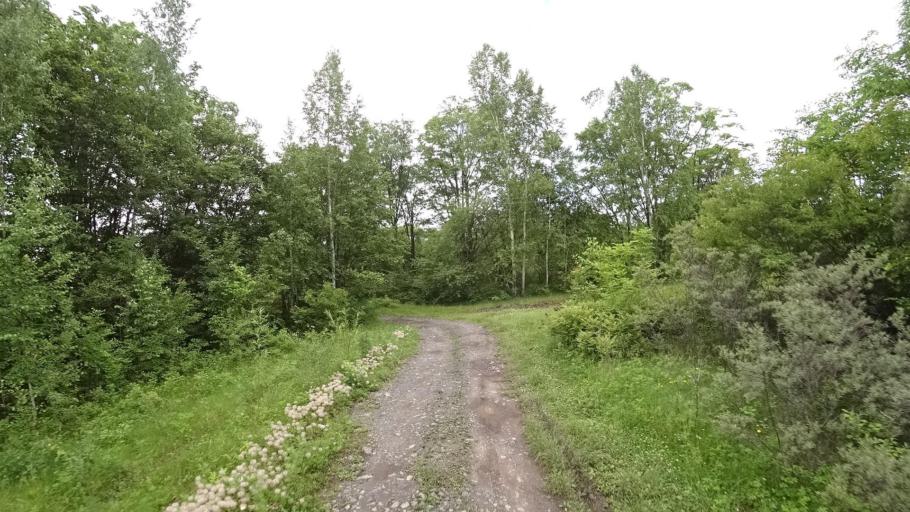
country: RU
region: Khabarovsk Krai
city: Amursk
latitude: 49.9050
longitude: 136.1326
